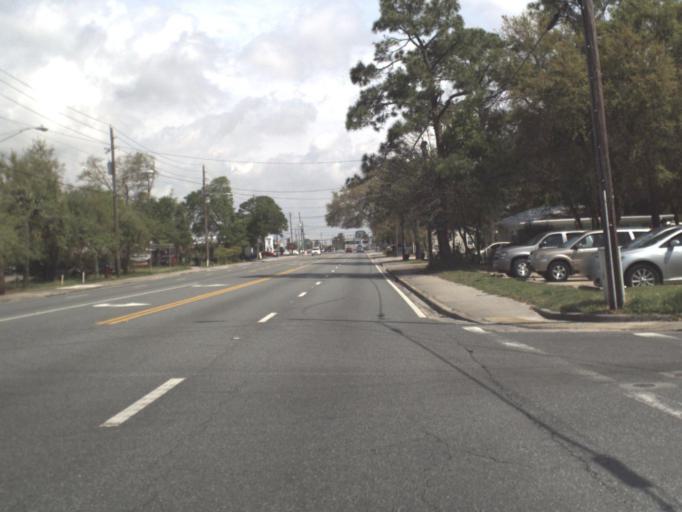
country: US
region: Florida
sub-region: Okaloosa County
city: Fort Walton Beach
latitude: 30.4088
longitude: -86.6130
